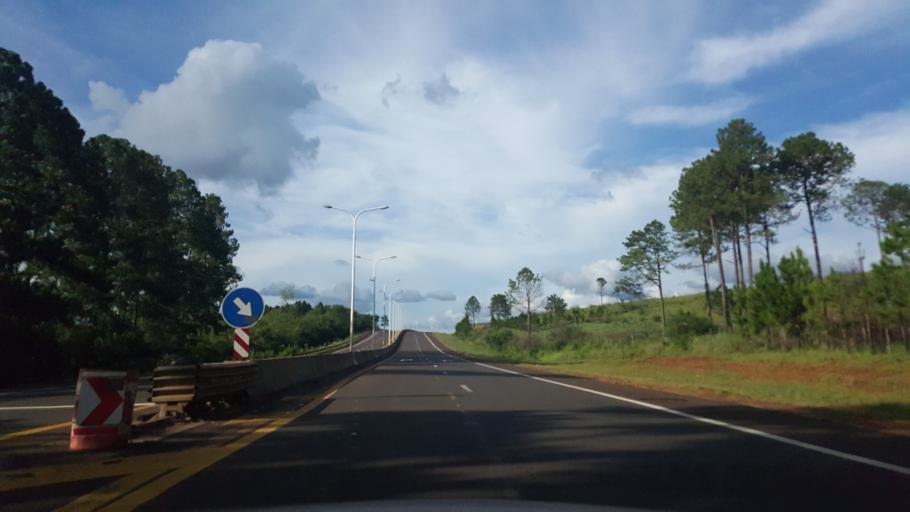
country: AR
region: Misiones
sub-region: Departamento de Candelaria
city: Loreto
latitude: -27.3198
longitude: -55.5456
